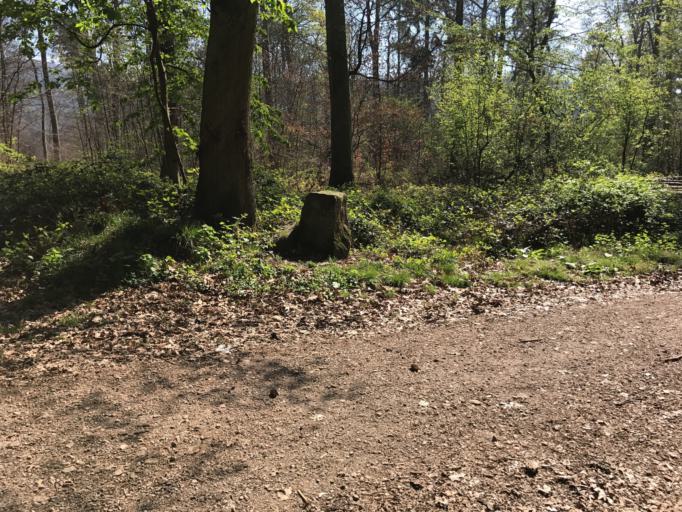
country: DE
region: Baden-Wuerttemberg
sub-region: Karlsruhe Region
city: Heidelberg
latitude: 49.3832
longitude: 8.6990
